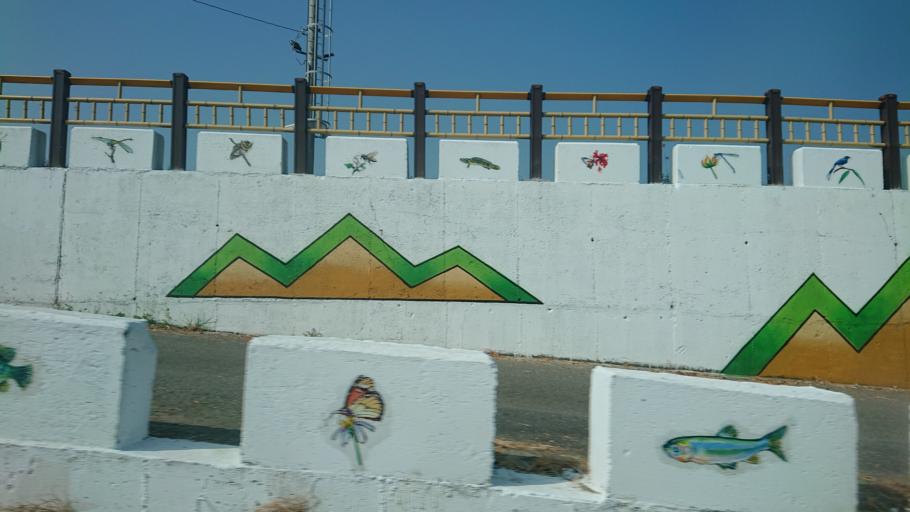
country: TW
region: Taiwan
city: Lugu
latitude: 23.7468
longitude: 120.6585
